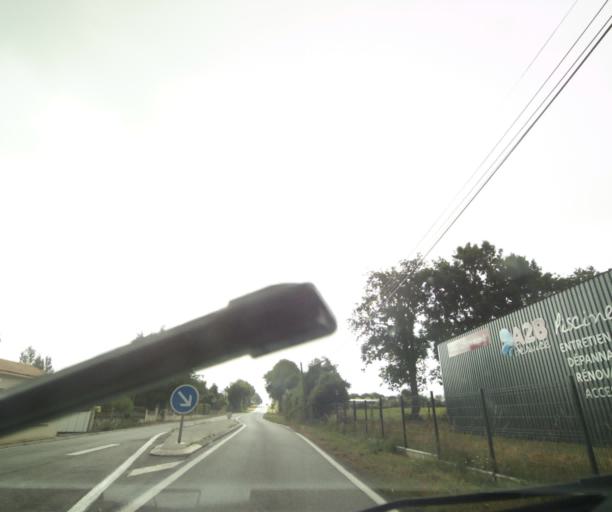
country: FR
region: Pays de la Loire
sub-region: Departement de la Vendee
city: Avrille
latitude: 46.4685
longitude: -1.4839
